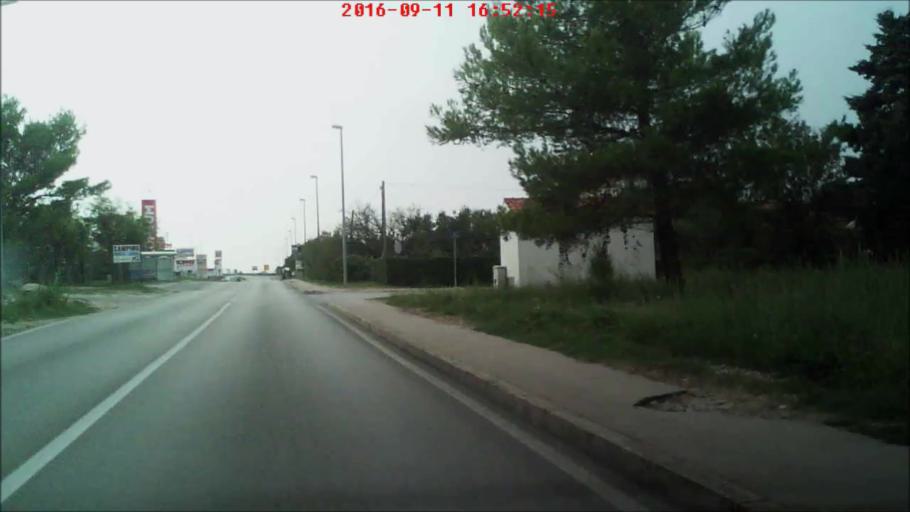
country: HR
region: Zadarska
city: Nin
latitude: 44.2415
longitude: 15.1734
